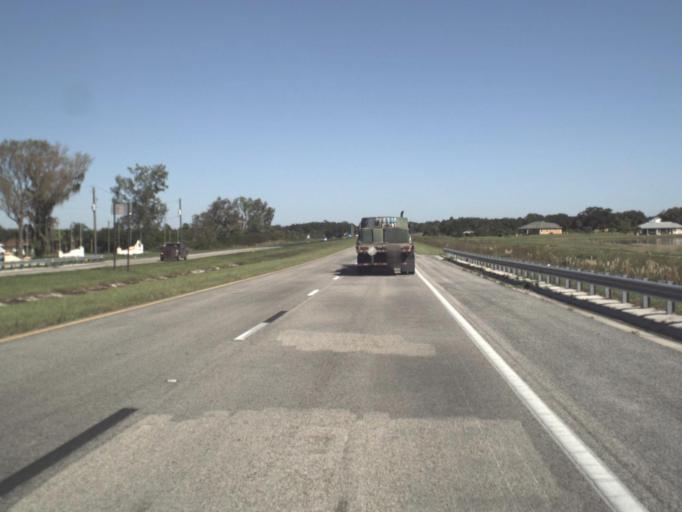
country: US
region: Florida
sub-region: Hendry County
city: Port LaBelle
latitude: 26.7629
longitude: -81.3994
